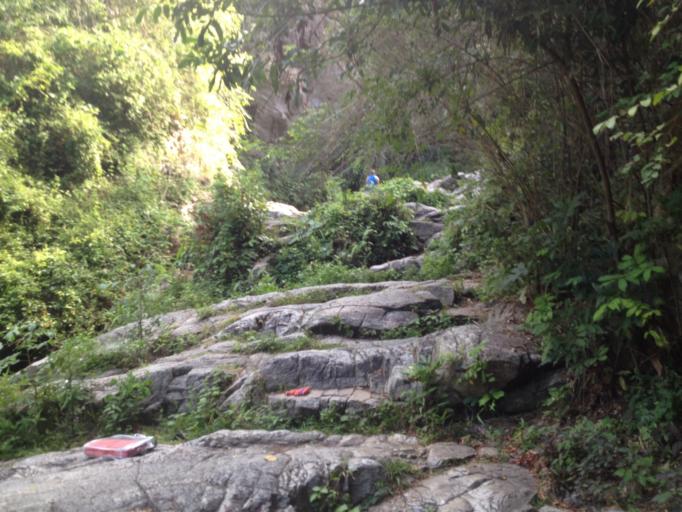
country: TH
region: Chiang Mai
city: Chiang Mai
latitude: 18.8116
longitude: 98.9437
